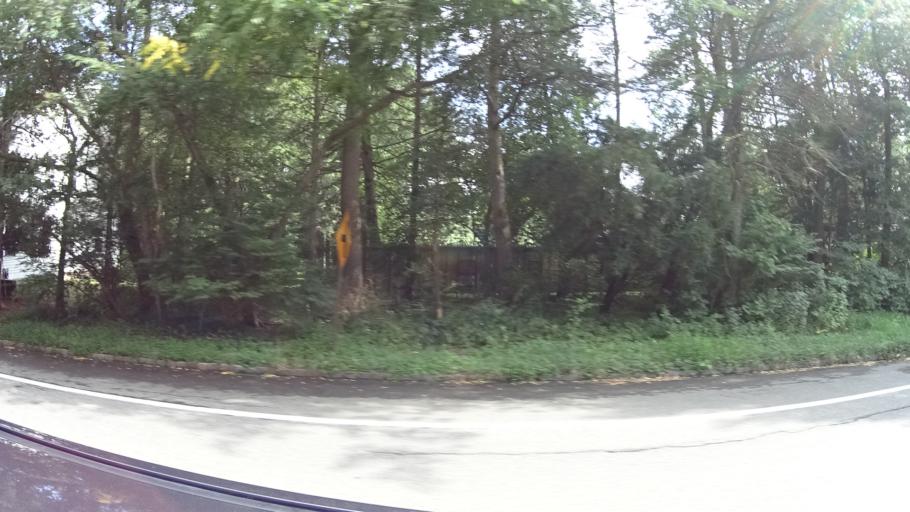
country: US
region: New Jersey
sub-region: Somerset County
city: Warren Township
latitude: 40.6664
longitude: -74.5109
